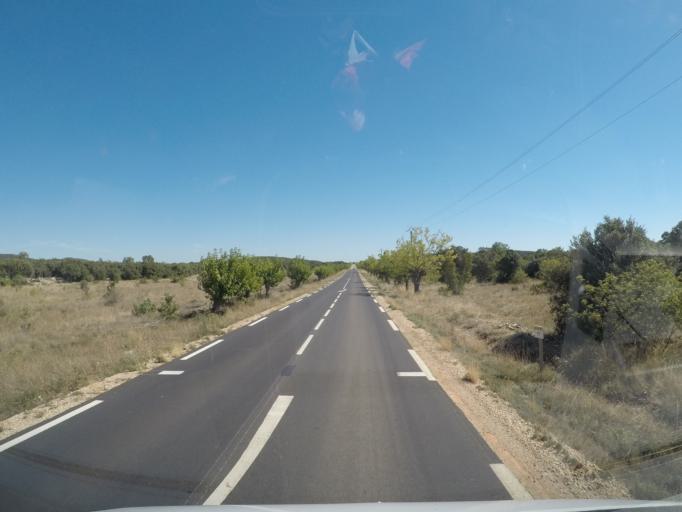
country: FR
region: Languedoc-Roussillon
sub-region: Departement de l'Herault
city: Aniane
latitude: 43.7267
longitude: 3.6539
